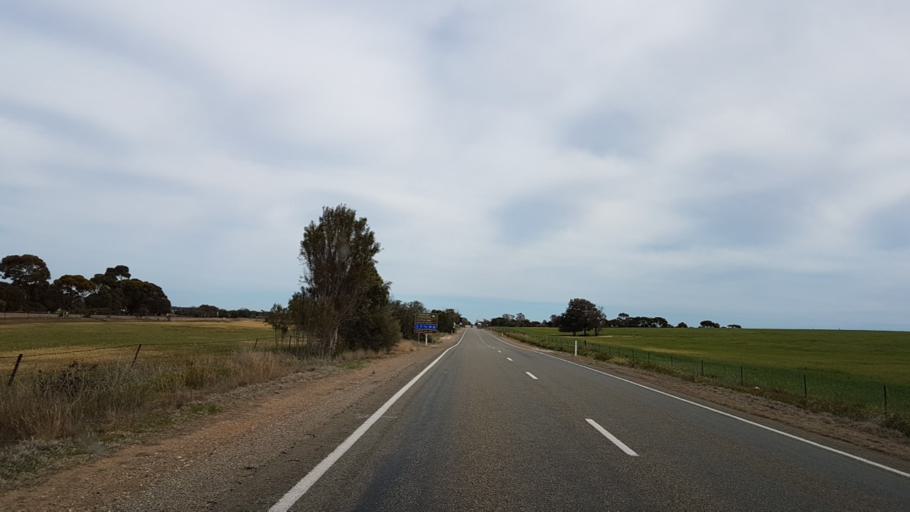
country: AU
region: South Australia
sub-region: Port Pirie City and Dists
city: Crystal Brook
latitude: -33.2523
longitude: 138.3636
